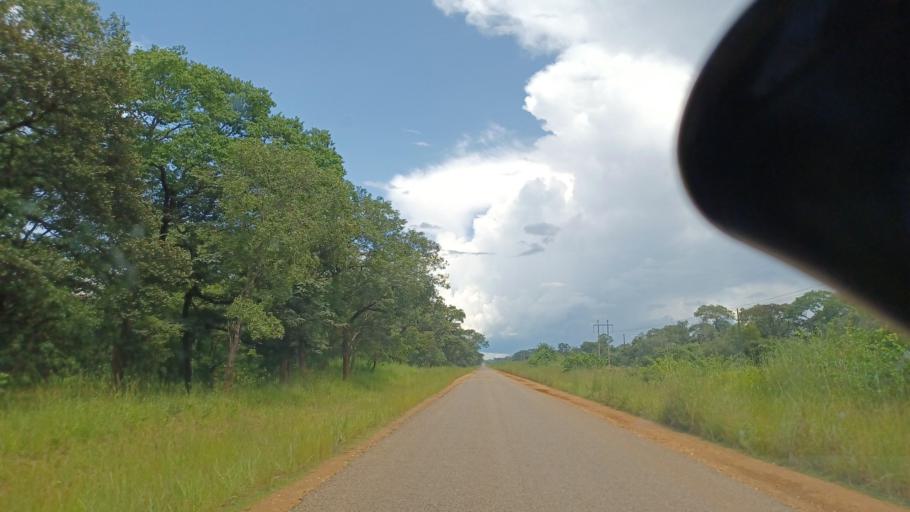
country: ZM
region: North-Western
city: Kasempa
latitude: -12.8819
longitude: 26.0462
